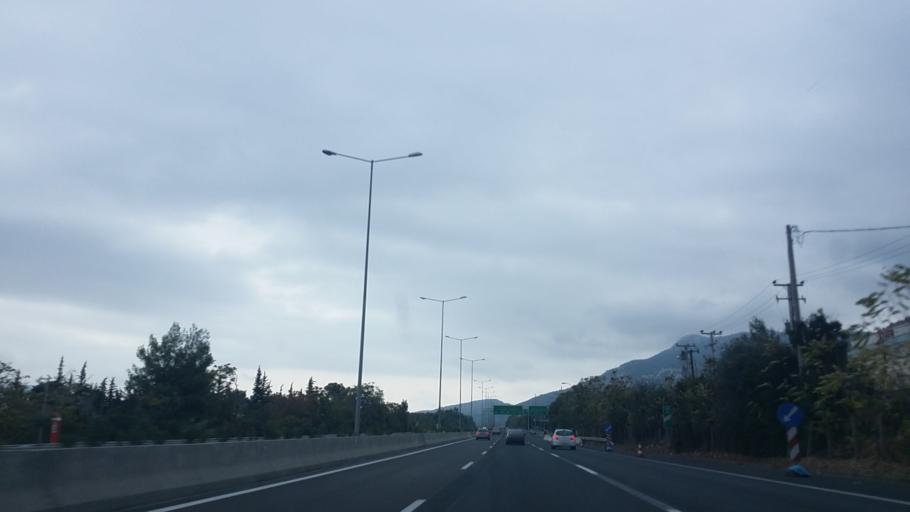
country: GR
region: Attica
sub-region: Nomarchia Anatolikis Attikis
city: Oropos
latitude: 38.2391
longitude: 23.7765
